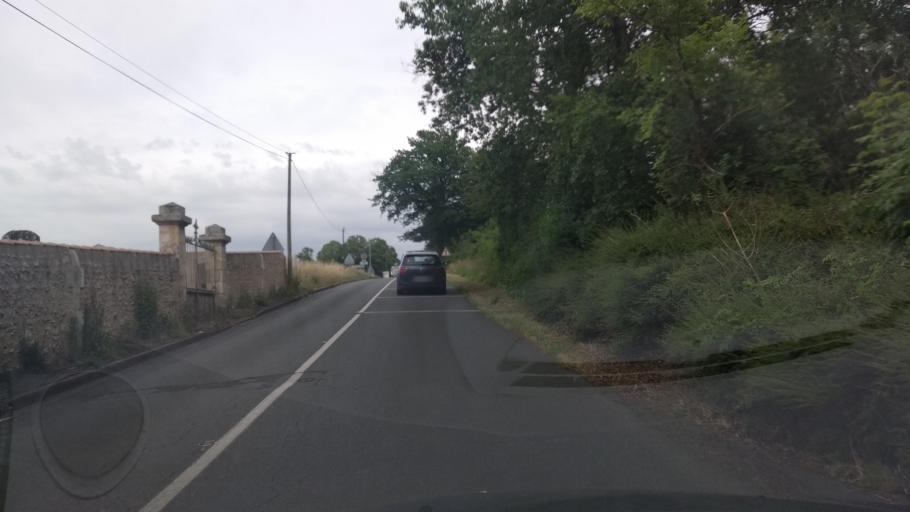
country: FR
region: Poitou-Charentes
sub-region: Departement de la Vienne
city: Biard
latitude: 46.5765
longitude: 0.3018
